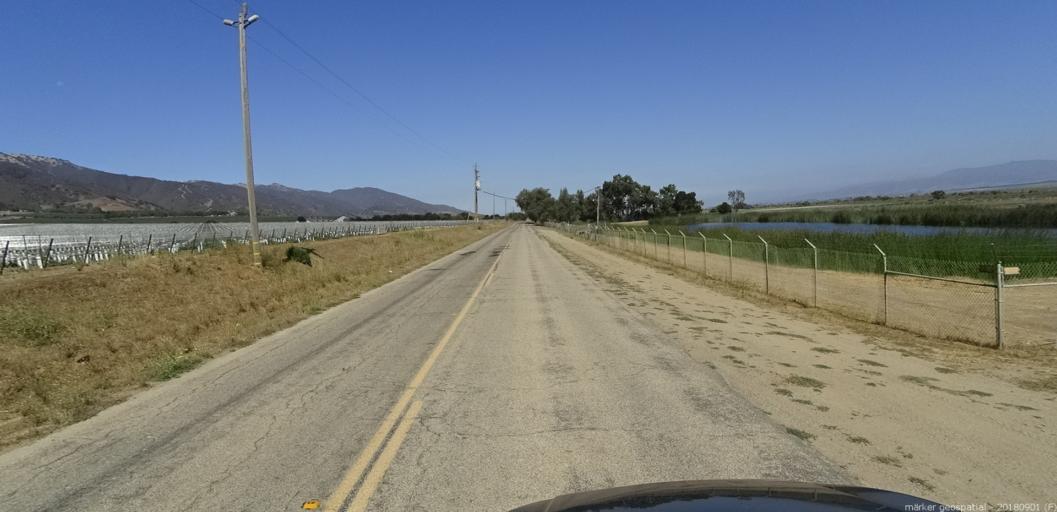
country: US
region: California
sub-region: Monterey County
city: Gonzales
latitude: 36.4939
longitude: -121.4966
